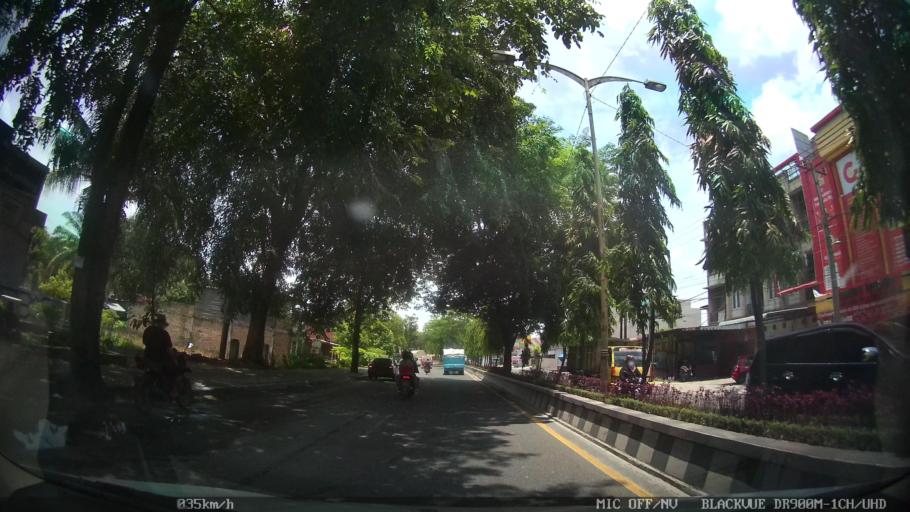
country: ID
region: North Sumatra
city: Percut
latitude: 3.5541
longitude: 98.8728
